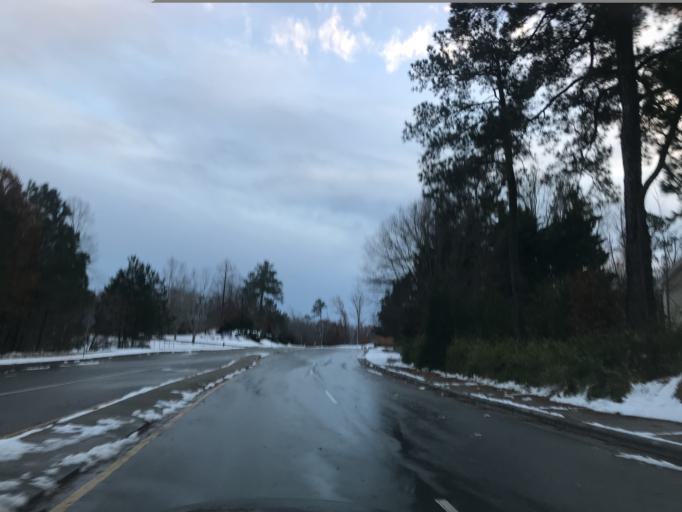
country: US
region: North Carolina
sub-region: Wake County
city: Rolesville
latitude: 35.8714
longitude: -78.5383
